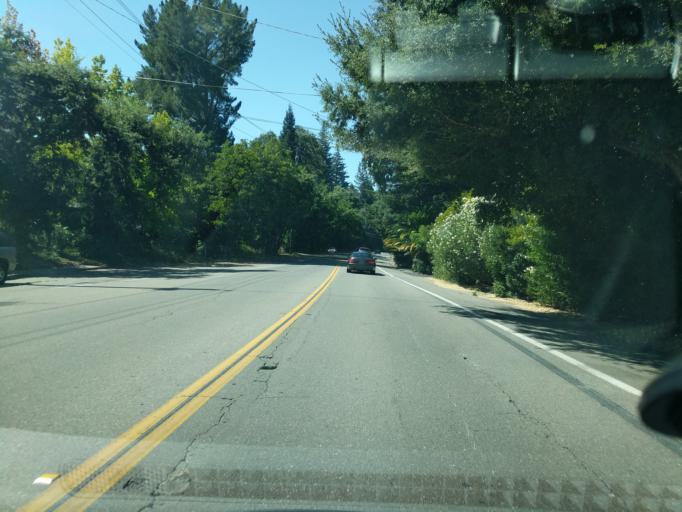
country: US
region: California
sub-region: Contra Costa County
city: Danville
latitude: 37.8307
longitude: -122.0117
